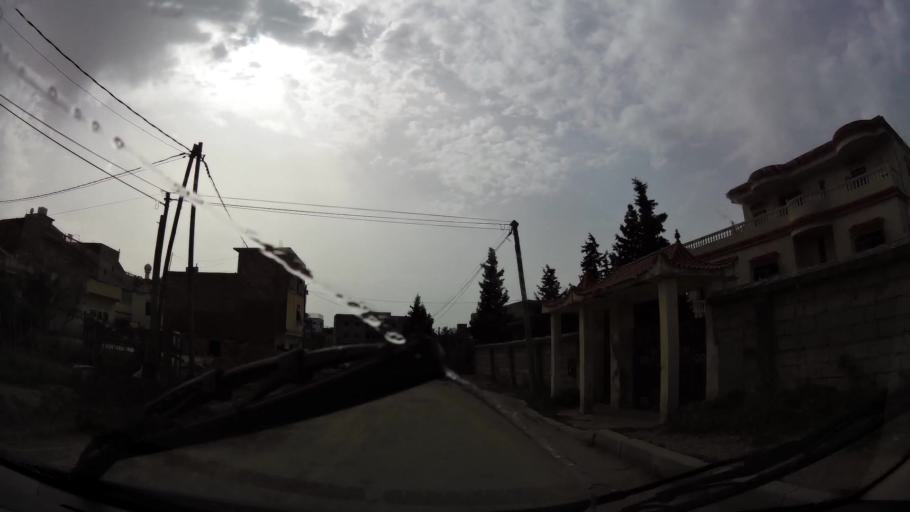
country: MA
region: Tanger-Tetouan
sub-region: Tanger-Assilah
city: Boukhalef
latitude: 35.7019
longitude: -5.9024
